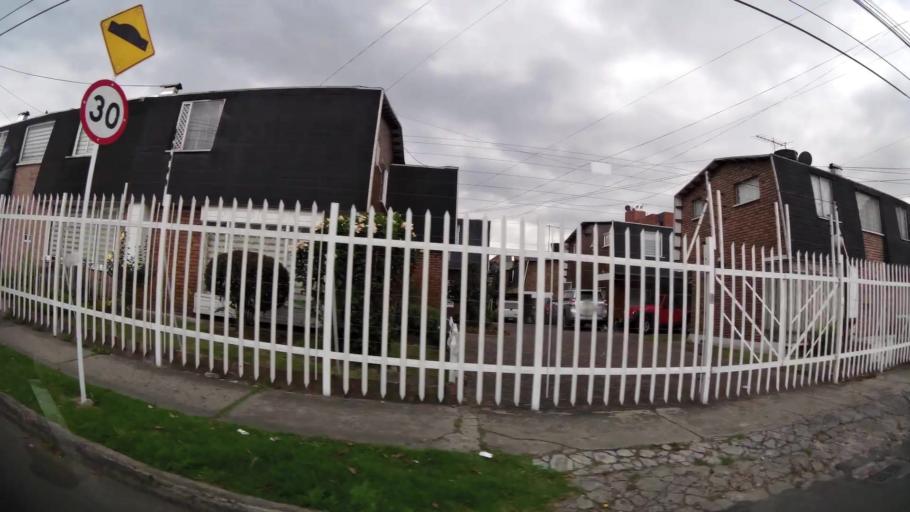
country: CO
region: Bogota D.C.
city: Bogota
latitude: 4.6624
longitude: -74.1180
